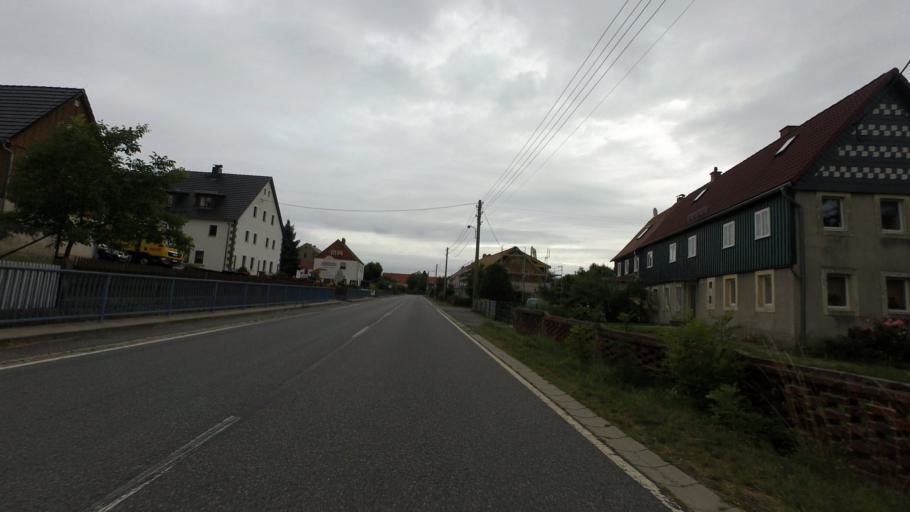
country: DE
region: Saxony
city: Berthelsdorf
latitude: 51.0523
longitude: 14.2262
